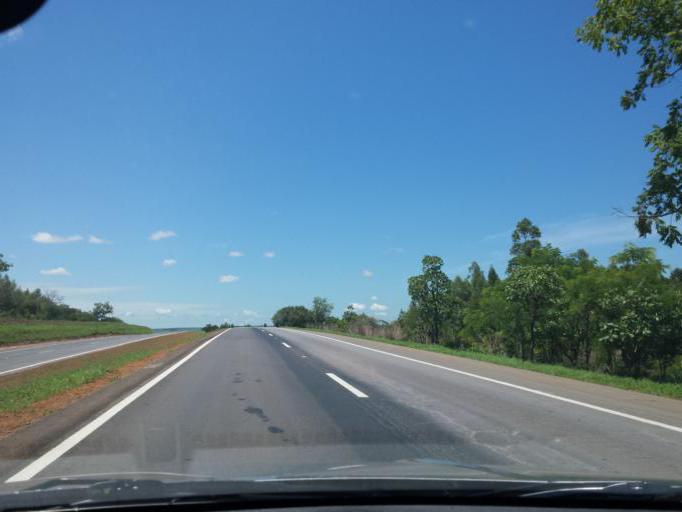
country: BR
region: Goias
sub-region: Luziania
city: Luziania
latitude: -16.4720
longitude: -47.8098
